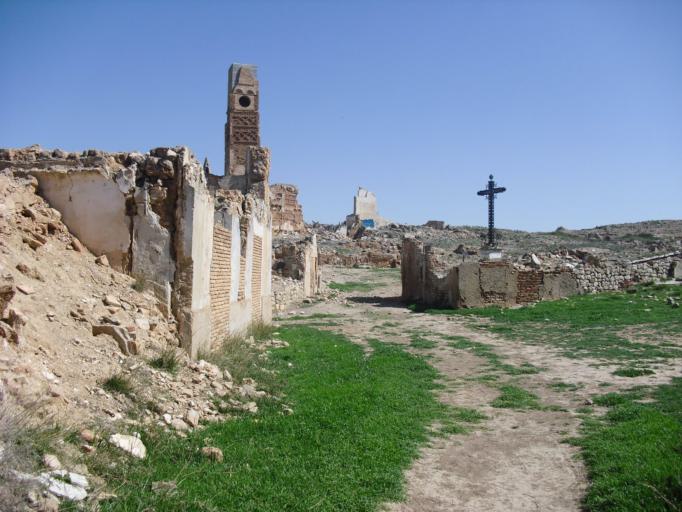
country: ES
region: Aragon
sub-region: Provincia de Zaragoza
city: Belchite
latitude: 41.3005
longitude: -0.7481
